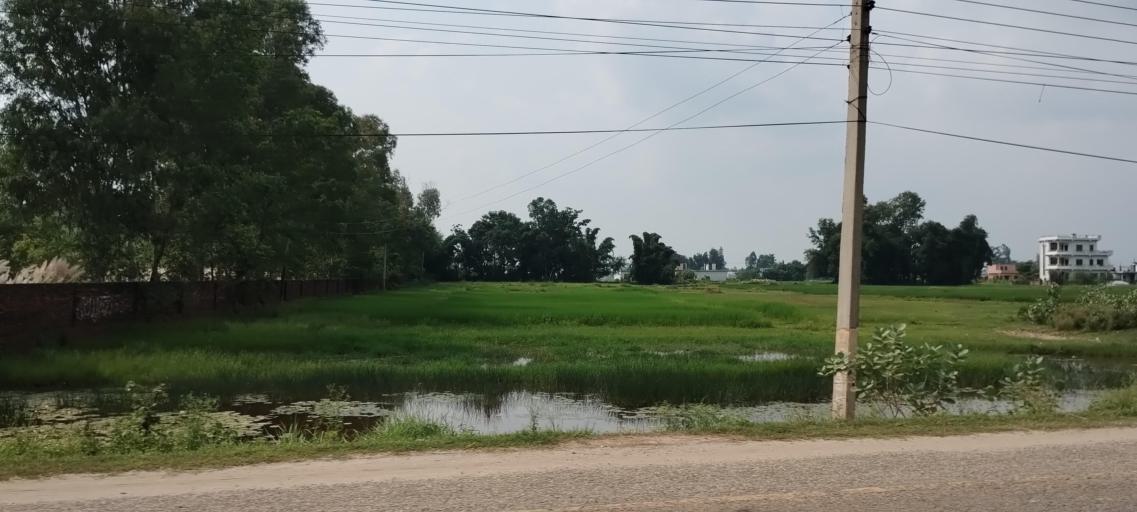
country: NP
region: Mid Western
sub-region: Bheri Zone
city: Nepalgunj
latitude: 28.1684
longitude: 81.6755
